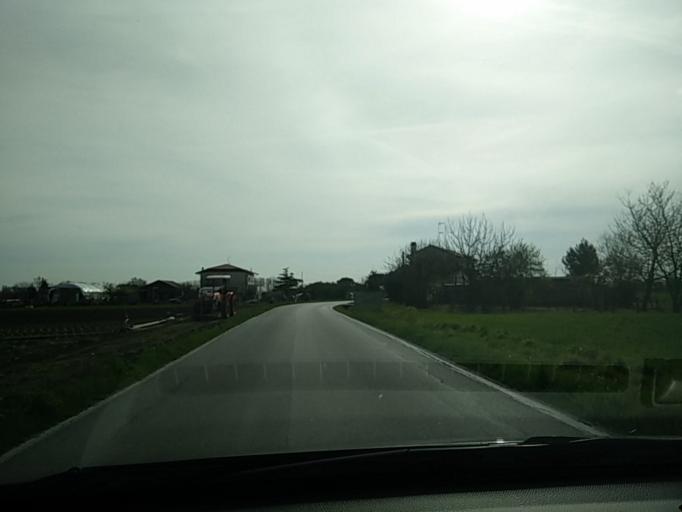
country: IT
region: Emilia-Romagna
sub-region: Provincia di Rimini
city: Santa Giustina
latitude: 44.0847
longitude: 12.4841
